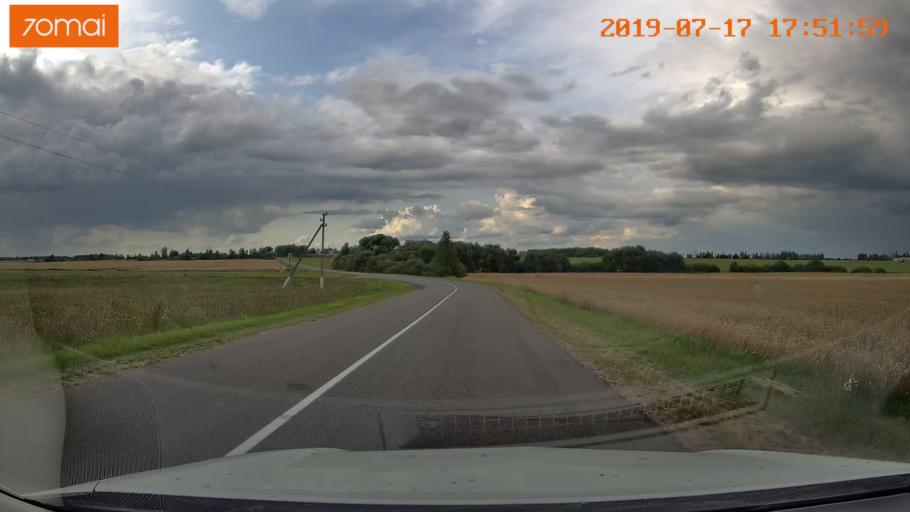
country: BY
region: Mogilev
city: Hlusha
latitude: 53.1597
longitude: 28.7866
